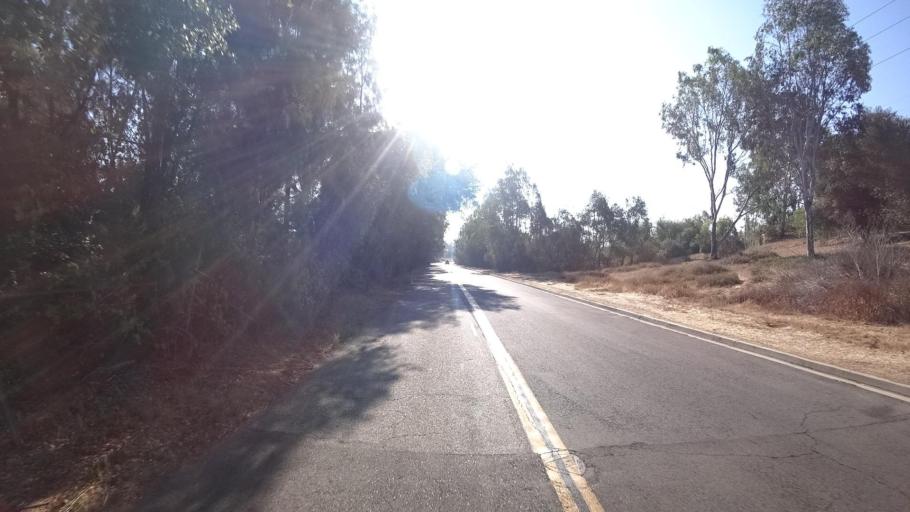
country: US
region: California
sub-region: San Diego County
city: Bonsall
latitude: 33.3150
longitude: -117.2579
